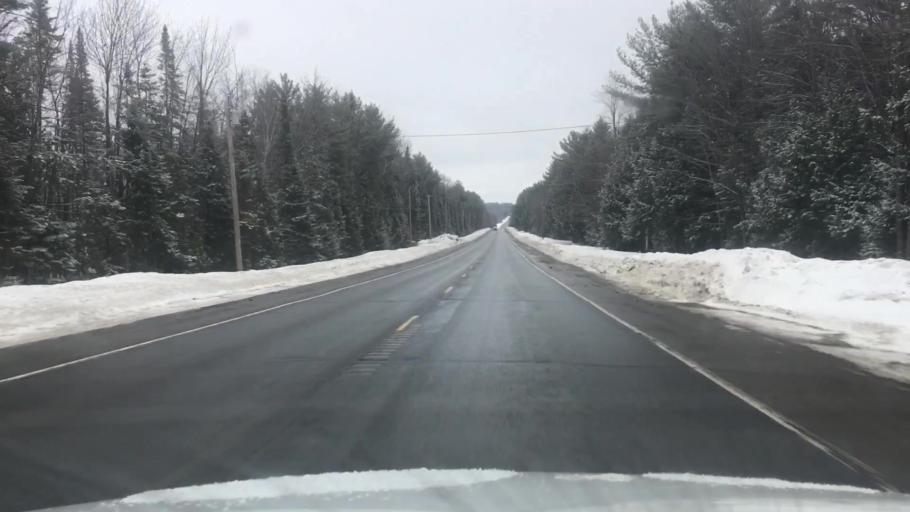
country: US
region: Maine
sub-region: Franklin County
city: New Sharon
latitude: 44.6418
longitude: -69.9883
